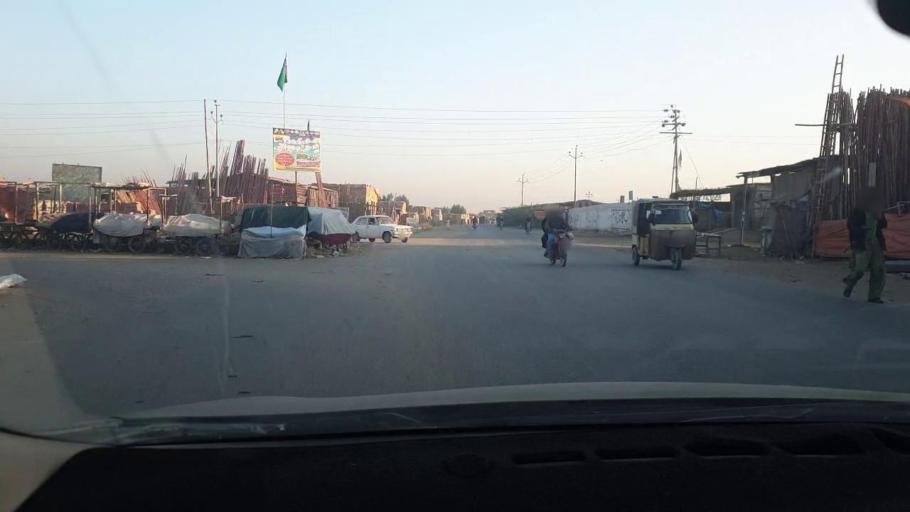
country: PK
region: Sindh
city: Malir Cantonment
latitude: 24.9964
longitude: 67.1428
